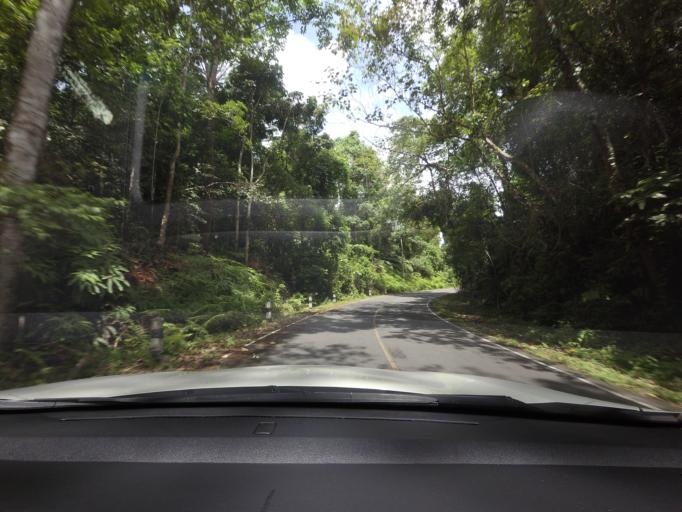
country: TH
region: Nakhon Nayok
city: Pak Phli
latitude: 14.3332
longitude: 101.3561
